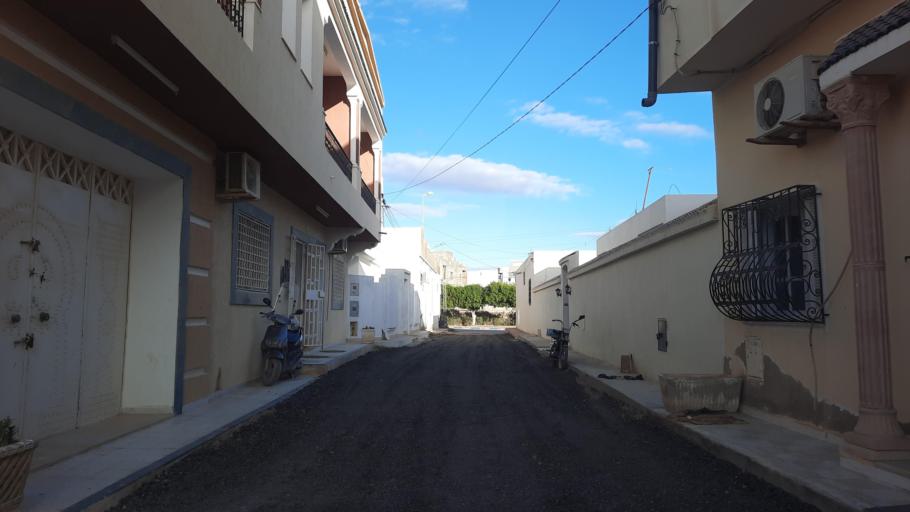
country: TN
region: Al Mahdiyah
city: El Jem
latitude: 35.2867
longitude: 10.7048
